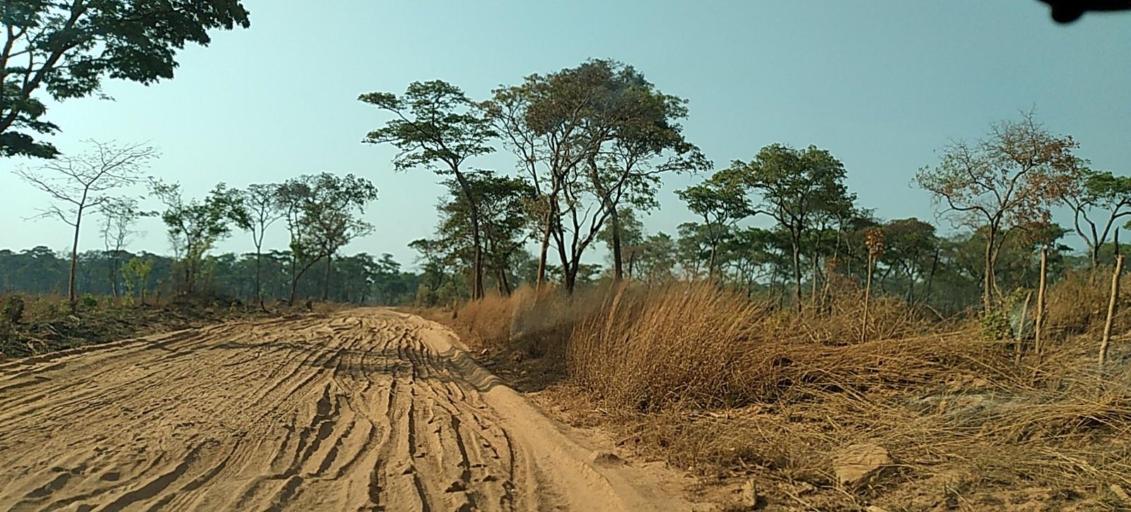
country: ZM
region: North-Western
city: Kasempa
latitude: -13.6237
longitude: 25.9825
